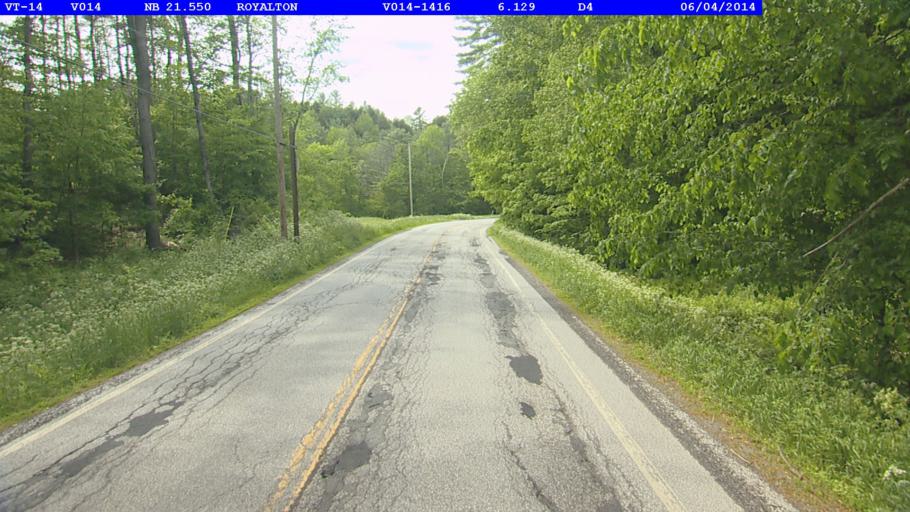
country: US
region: Vermont
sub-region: Orange County
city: Randolph
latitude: 43.8297
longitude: -72.5695
